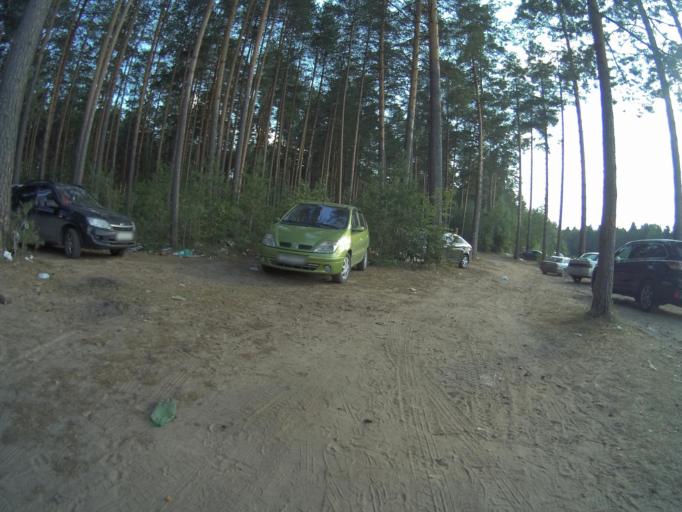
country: RU
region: Vladimir
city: Golovino
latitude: 56.0328
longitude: 40.4110
